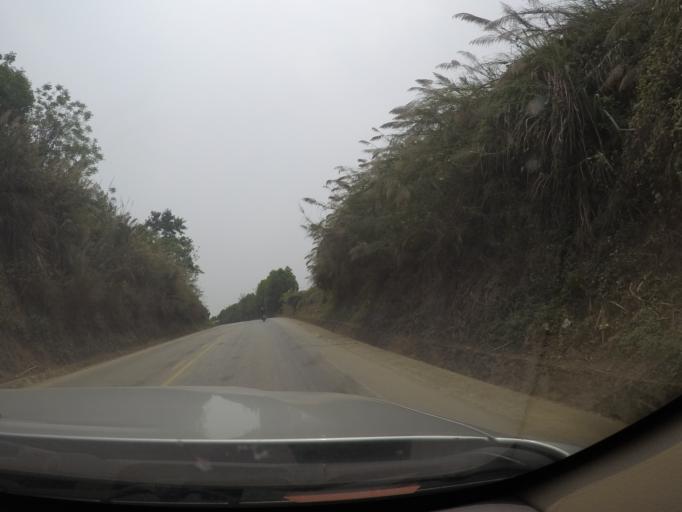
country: VN
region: Thanh Hoa
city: Thi Tran Thuong Xuan
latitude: 19.9000
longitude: 105.3986
